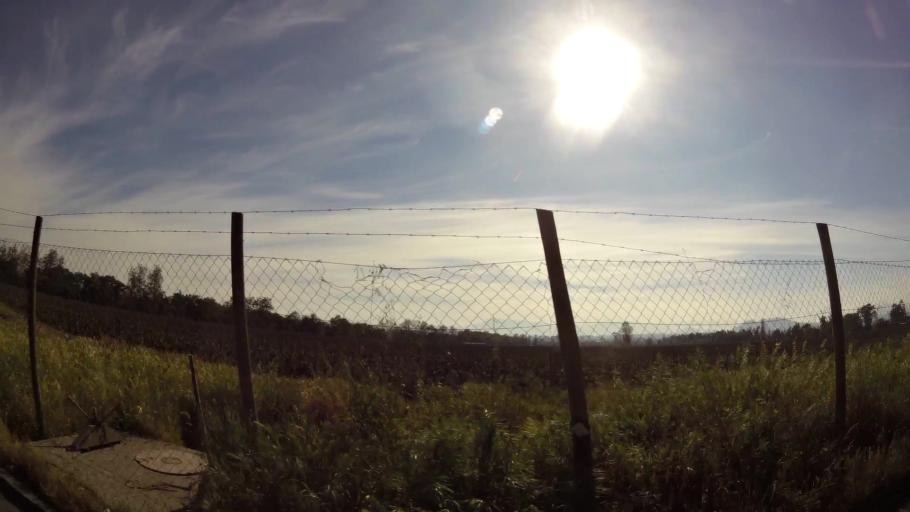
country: CL
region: Santiago Metropolitan
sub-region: Provincia de Santiago
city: Villa Presidente Frei, Nunoa, Santiago, Chile
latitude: -33.4901
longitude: -70.5590
